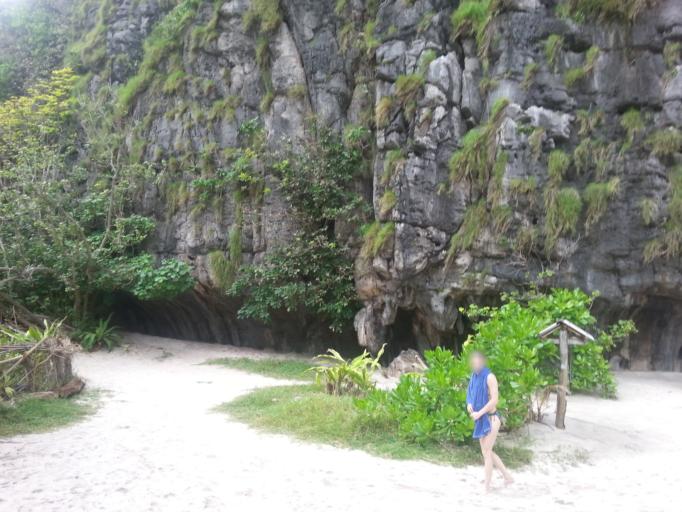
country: TH
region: Krabi
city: Saladan
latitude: 7.6763
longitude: 98.7655
